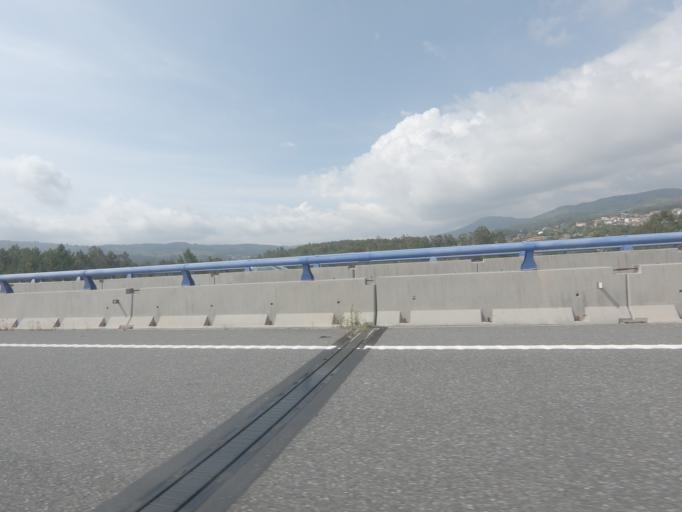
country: ES
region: Galicia
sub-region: Provincia de Pontevedra
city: Covelo
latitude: 42.2009
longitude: -8.2867
